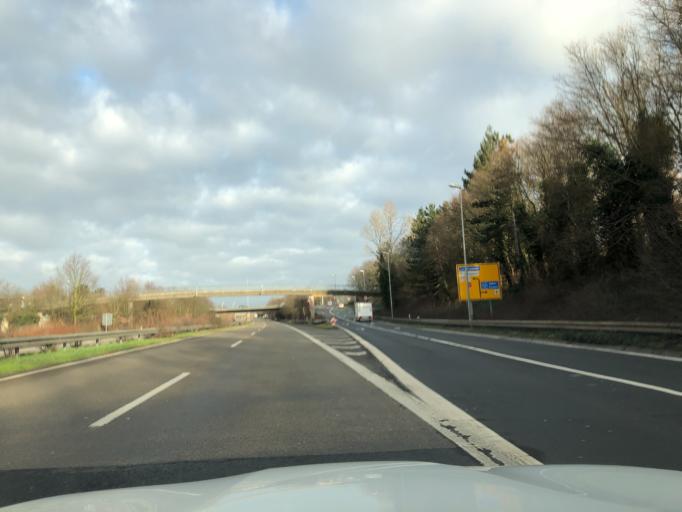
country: DE
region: North Rhine-Westphalia
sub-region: Regierungsbezirk Dusseldorf
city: Dusseldorf
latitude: 51.2686
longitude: 6.7523
